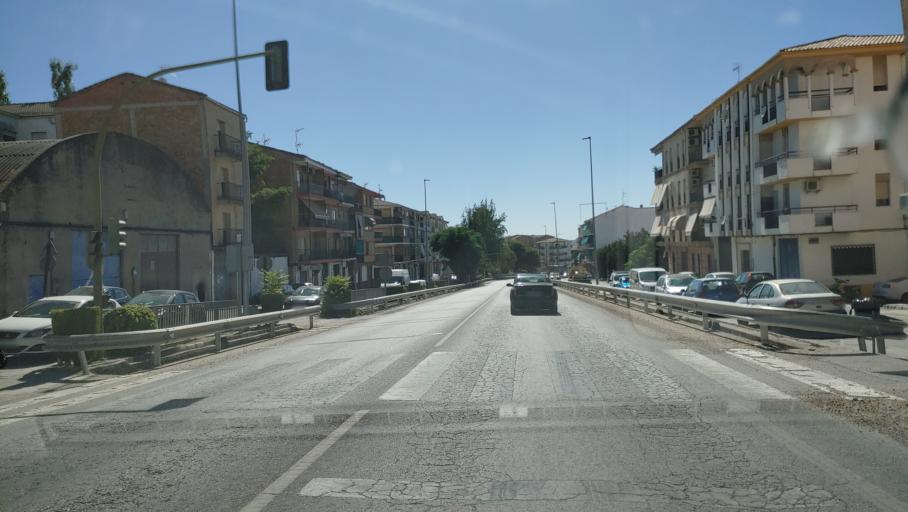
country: ES
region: Andalusia
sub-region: Provincia de Jaen
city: Villacarrillo
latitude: 38.1190
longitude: -3.0802
